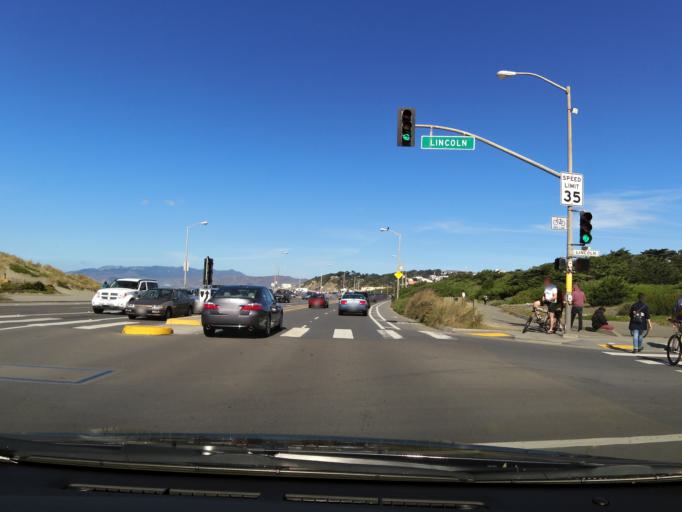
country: US
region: California
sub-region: San Mateo County
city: Daly City
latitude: 37.7641
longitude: -122.5103
